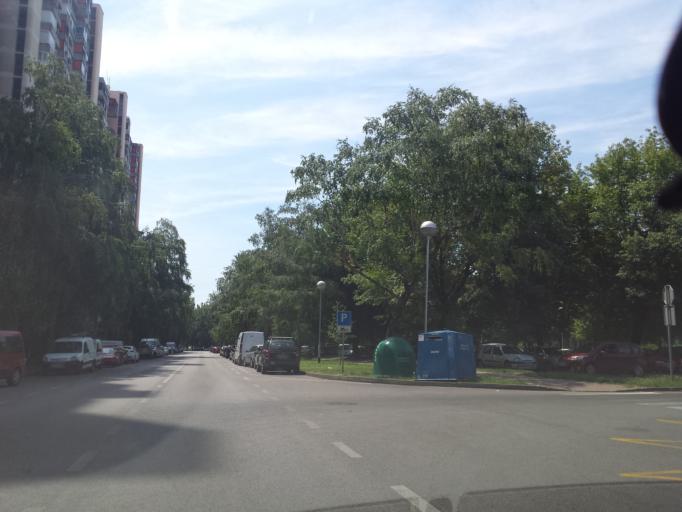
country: HR
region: Grad Zagreb
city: Novi Zagreb
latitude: 45.7718
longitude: 15.9941
